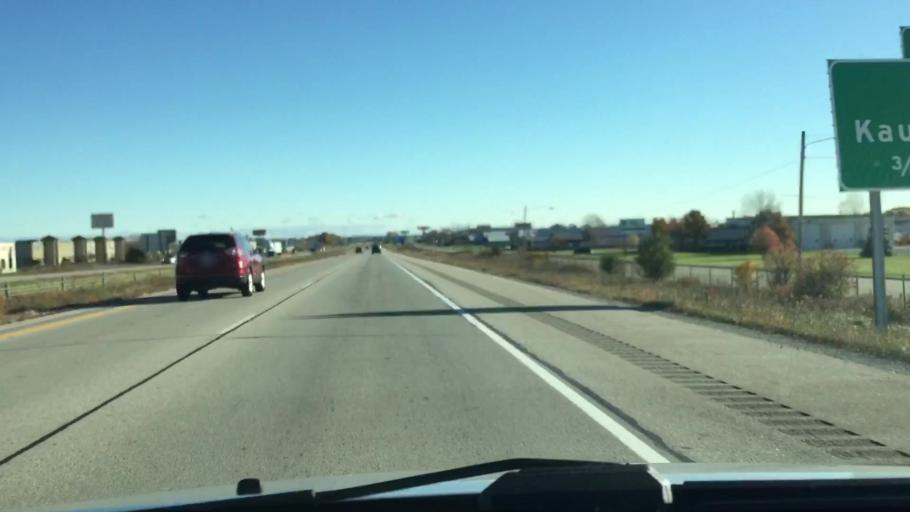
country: US
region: Wisconsin
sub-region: Outagamie County
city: Kaukauna
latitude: 44.3014
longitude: -88.2644
